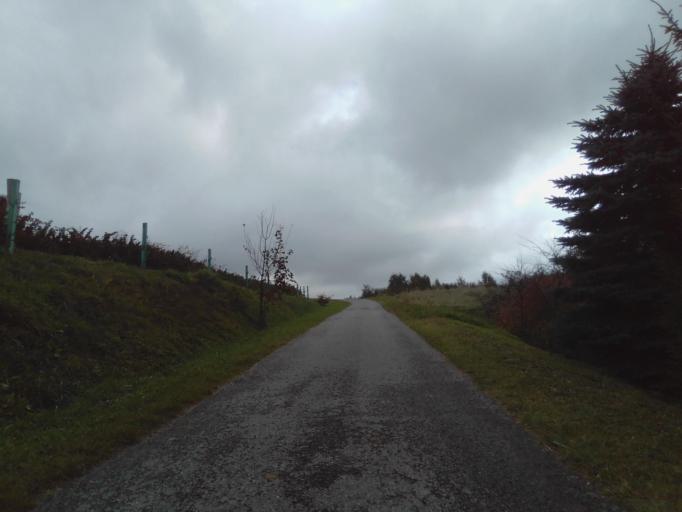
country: PL
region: Subcarpathian Voivodeship
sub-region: Powiat strzyzowski
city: Gwoznica Gorna
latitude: 49.8338
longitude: 22.0177
